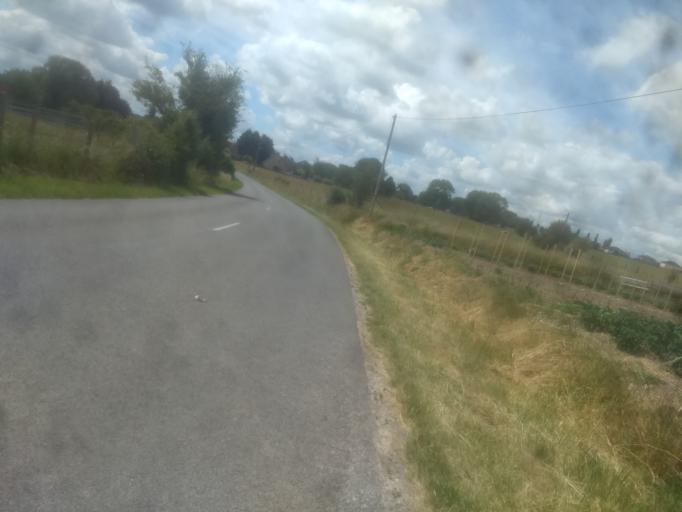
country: FR
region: Nord-Pas-de-Calais
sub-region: Departement du Pas-de-Calais
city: Mont-Saint-Eloi
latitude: 50.3466
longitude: 2.6661
